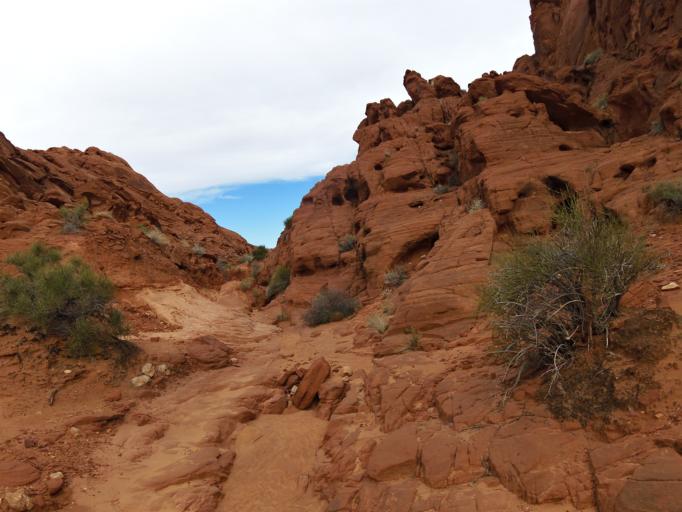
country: US
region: Nevada
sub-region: Clark County
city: Moapa Valley
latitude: 36.4482
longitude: -114.5102
